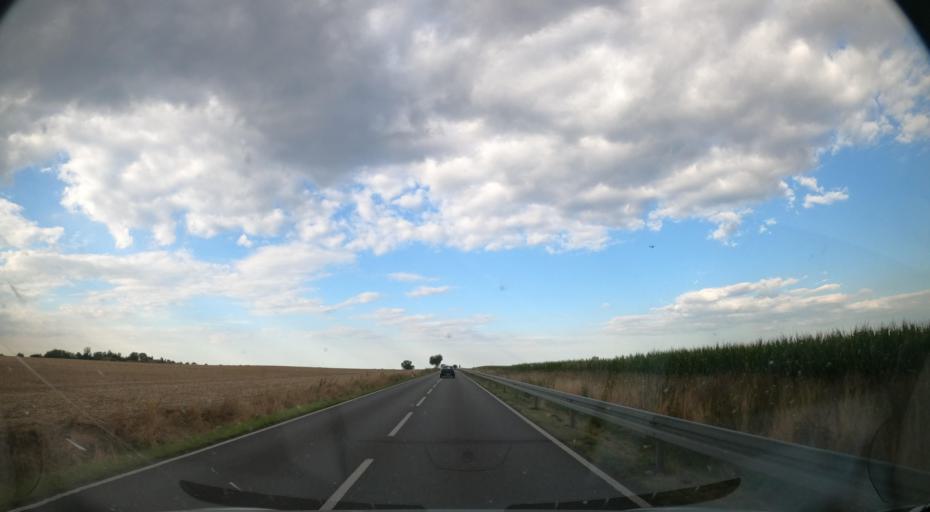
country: DE
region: Mecklenburg-Vorpommern
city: Pasewalk
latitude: 53.5033
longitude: 13.9572
